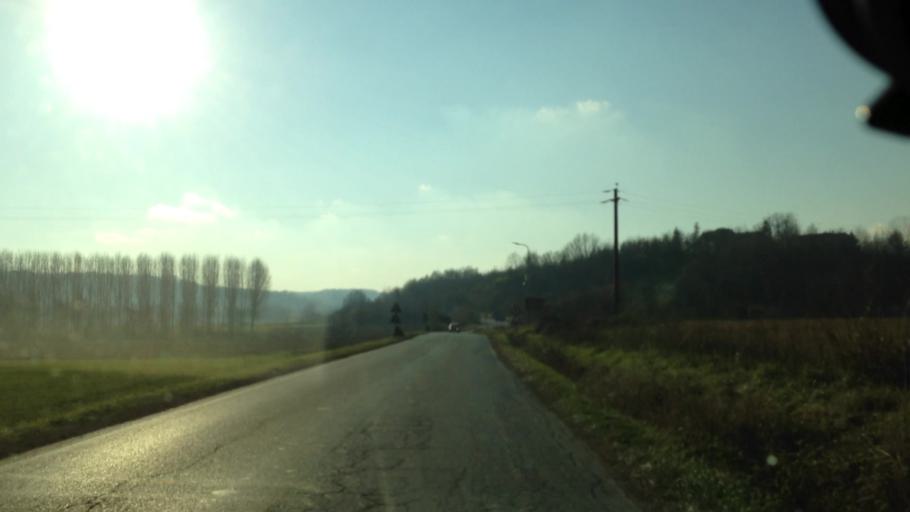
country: IT
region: Piedmont
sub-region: Provincia di Alessandria
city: Masio
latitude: 44.8459
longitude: 8.3962
